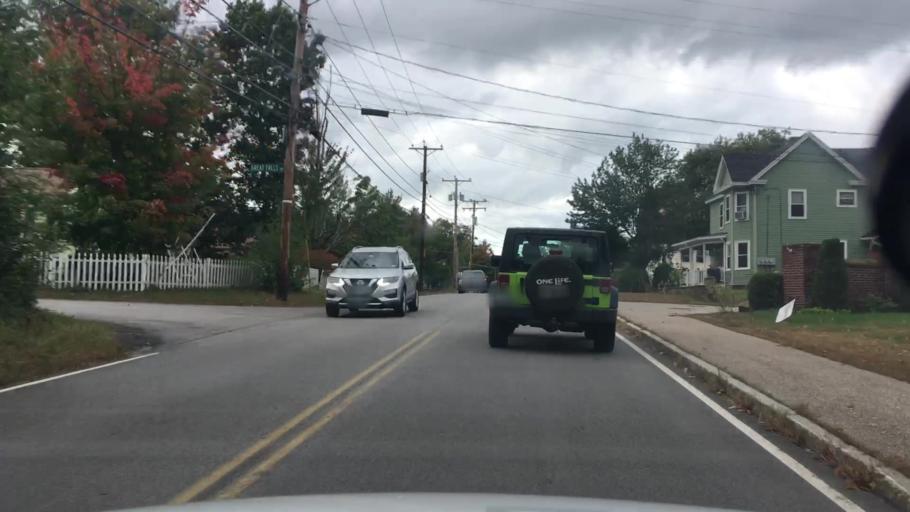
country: US
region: New Hampshire
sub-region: Strafford County
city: Rochester
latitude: 43.2925
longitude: -70.9713
